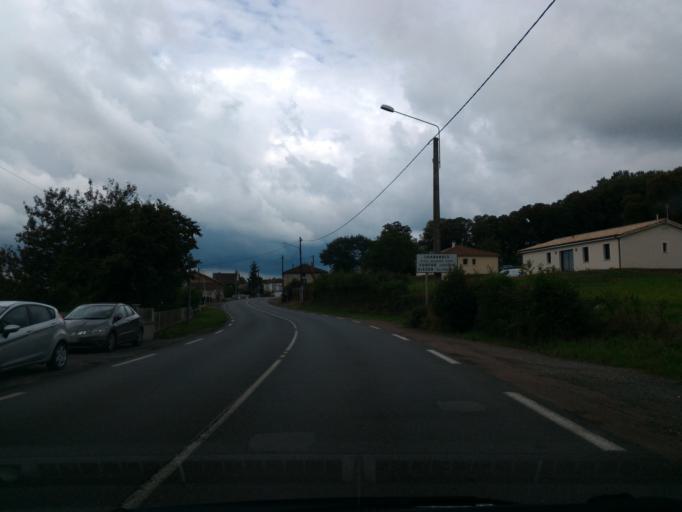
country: FR
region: Poitou-Charentes
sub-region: Departement de la Charente
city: Chabanais
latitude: 45.8784
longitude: 0.7282
